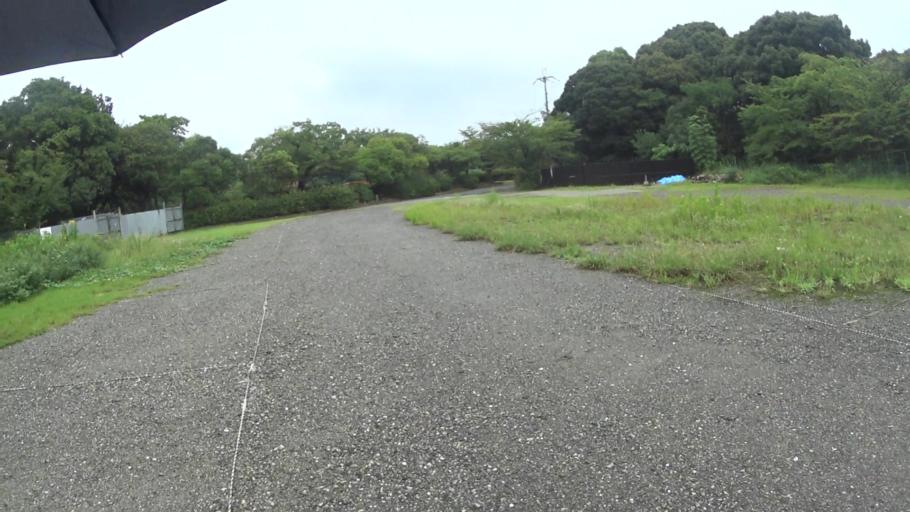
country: JP
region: Osaka
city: Takaishi
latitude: 34.5035
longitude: 135.4972
